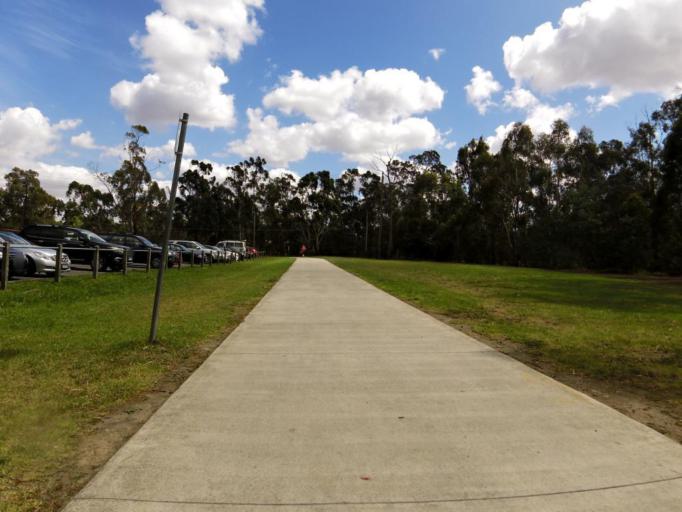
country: AU
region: Victoria
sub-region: Nillumbik
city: Eltham
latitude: -37.7231
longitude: 145.1425
